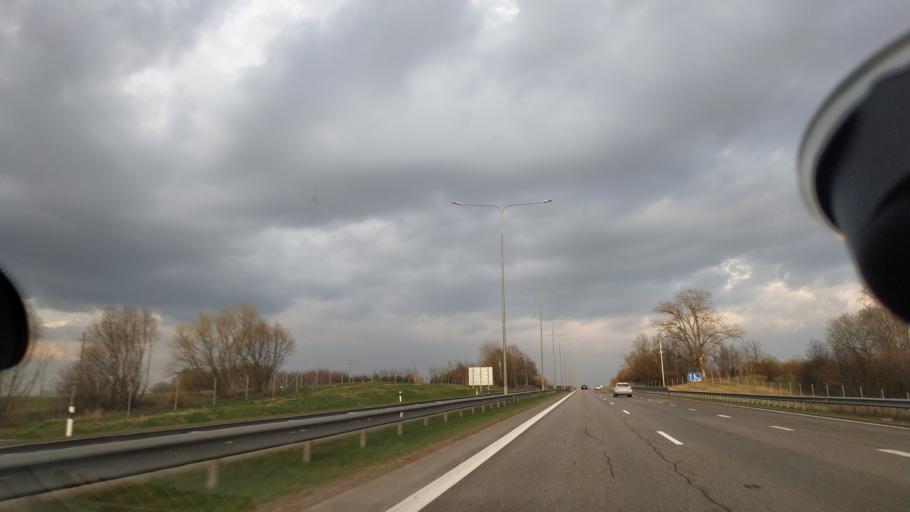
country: LT
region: Vilnius County
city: Elektrenai
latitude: 54.7893
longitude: 24.6805
